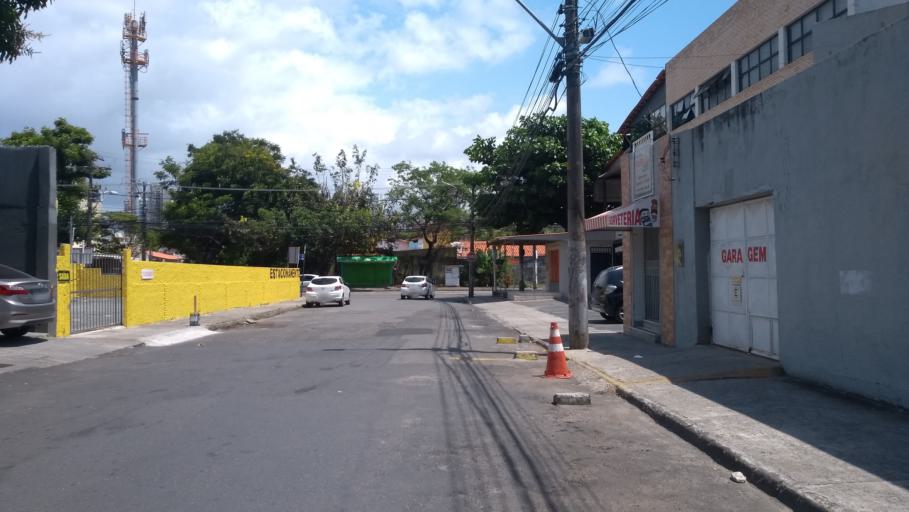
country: BR
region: Bahia
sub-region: Salvador
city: Salvador
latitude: -12.9906
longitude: -38.4571
